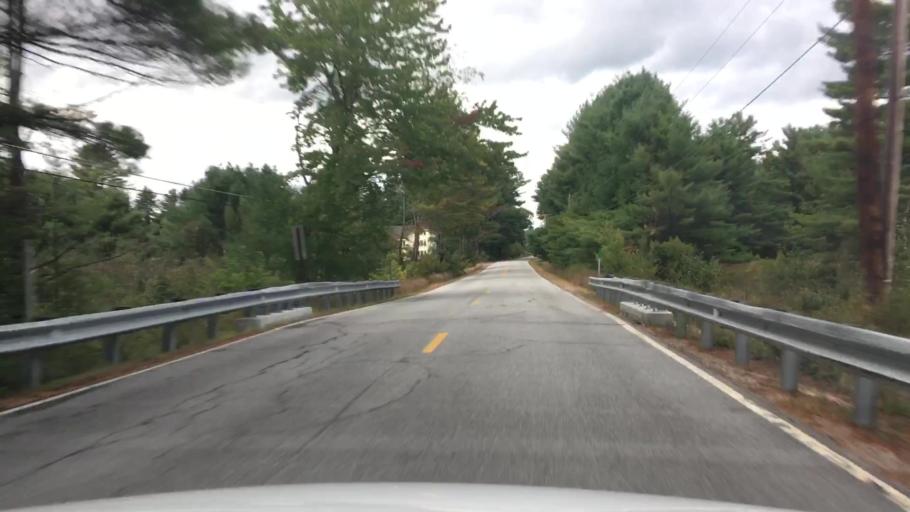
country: US
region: New Hampshire
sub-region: Carroll County
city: Effingham
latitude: 43.7062
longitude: -70.9819
